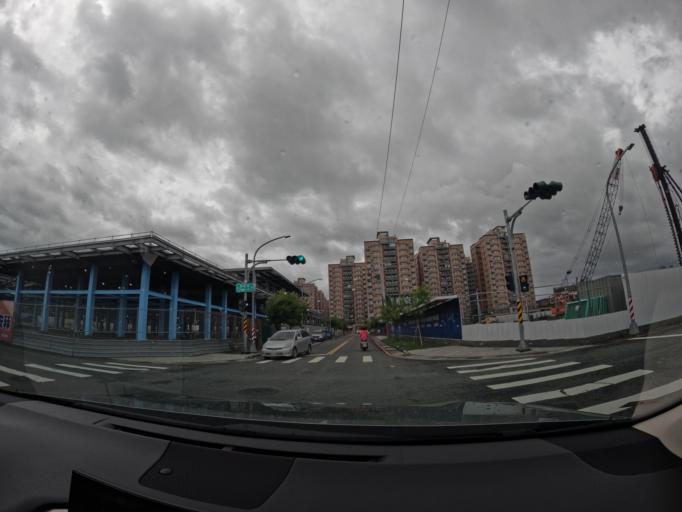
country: TW
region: Taiwan
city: Fengshan
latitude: 22.6323
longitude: 120.3720
